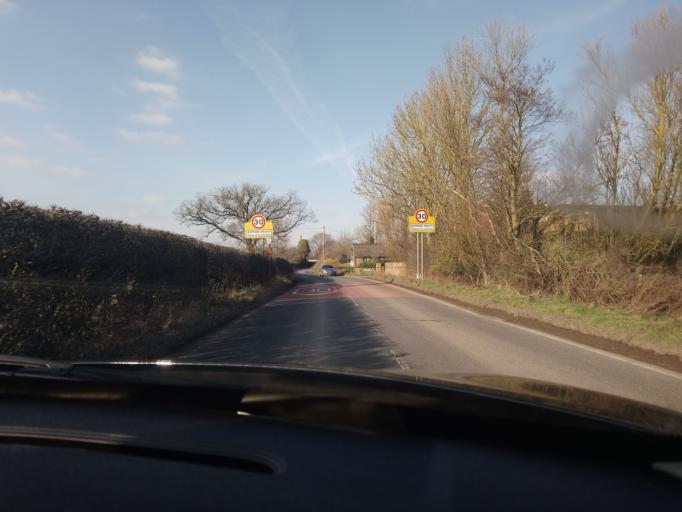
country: GB
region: England
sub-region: Shropshire
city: Bicton
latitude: 52.7667
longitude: -2.7797
